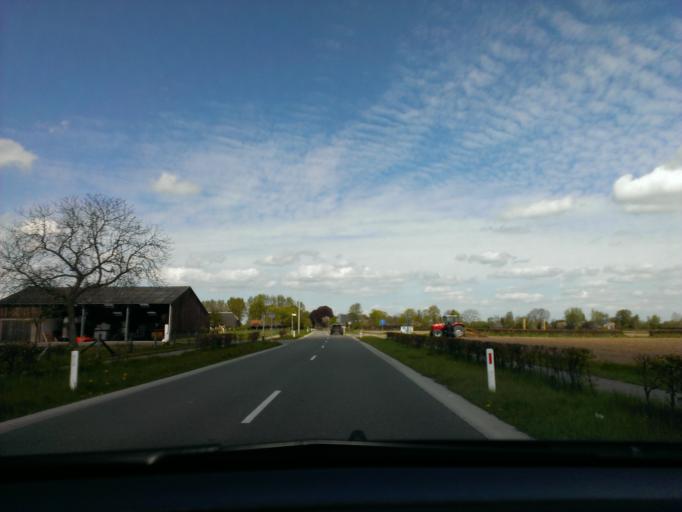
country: NL
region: Gelderland
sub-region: Gemeente Voorst
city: Twello
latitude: 52.2534
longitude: 6.1120
